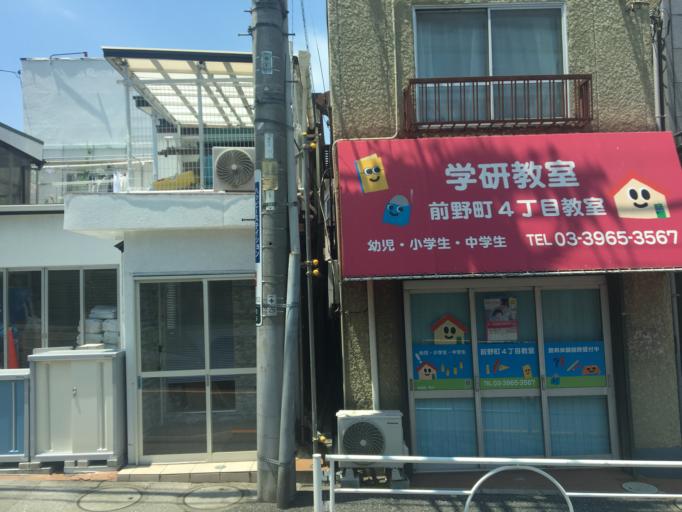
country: JP
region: Saitama
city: Kawaguchi
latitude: 35.7702
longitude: 139.6912
